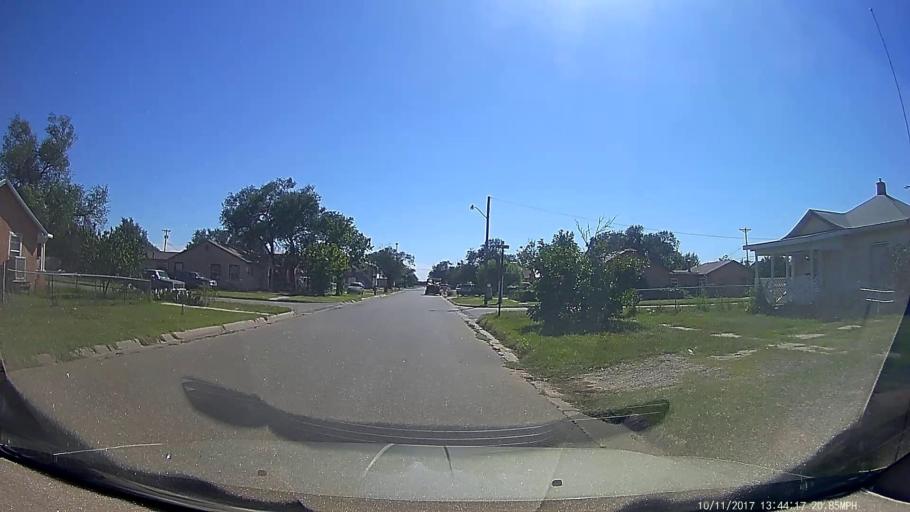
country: US
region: New Mexico
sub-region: Curry County
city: Clovis
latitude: 34.4016
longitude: -103.2119
